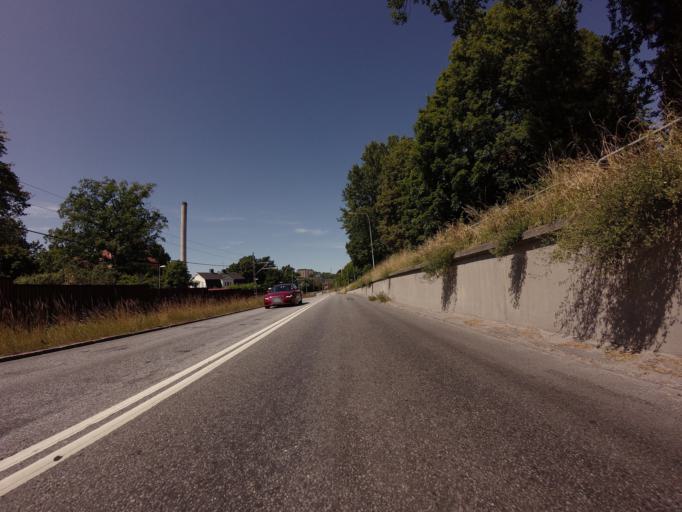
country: SE
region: Stockholm
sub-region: Nacka Kommun
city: Nacka
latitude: 59.3444
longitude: 18.1644
